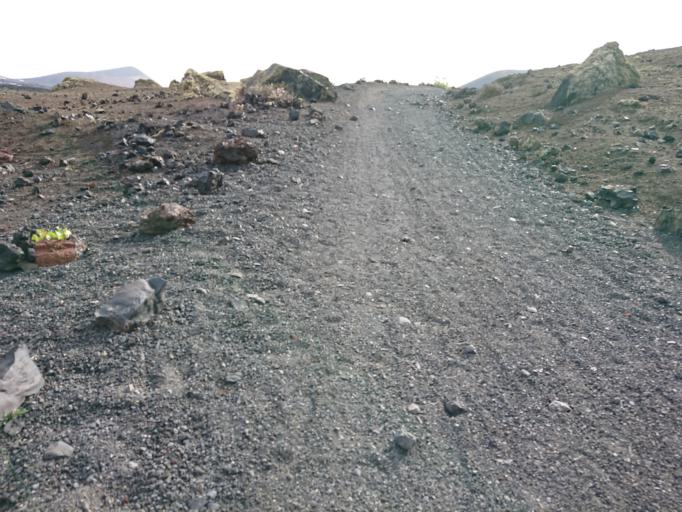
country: ES
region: Canary Islands
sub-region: Provincia de Las Palmas
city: Tias
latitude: 29.0064
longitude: -13.6756
